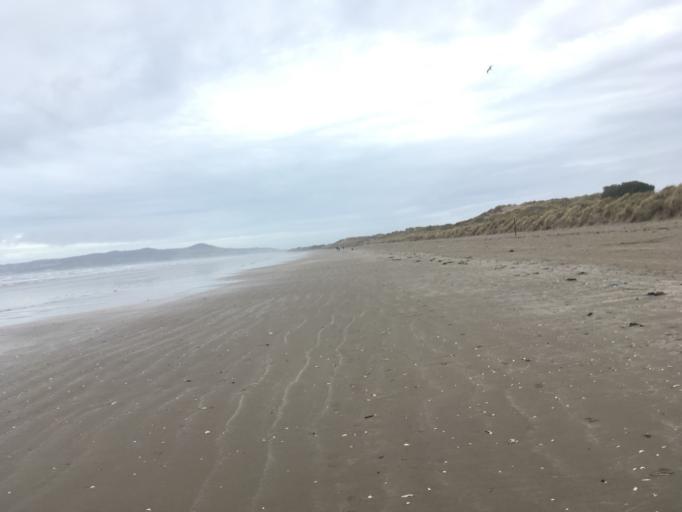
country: IE
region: Leinster
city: Portmarnock
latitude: 53.4222
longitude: -6.1218
